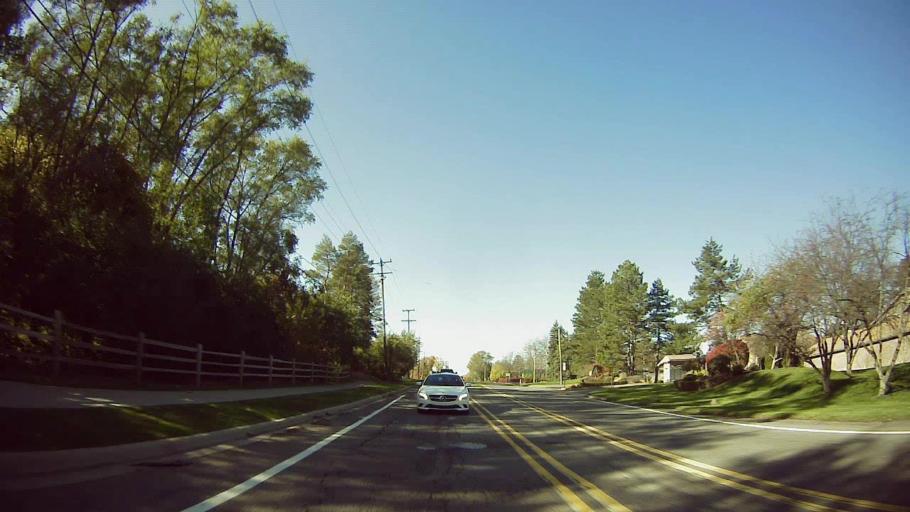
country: US
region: Michigan
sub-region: Oakland County
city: Franklin
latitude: 42.5439
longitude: -83.3187
